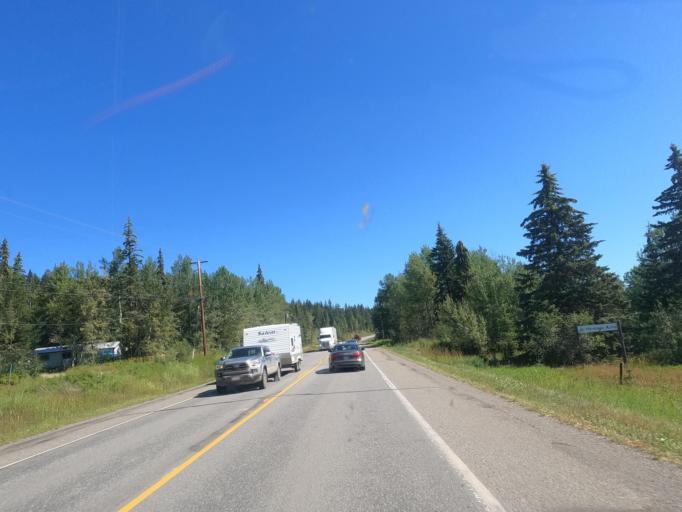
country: CA
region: British Columbia
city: Quesnel
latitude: 53.0451
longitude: -122.4681
